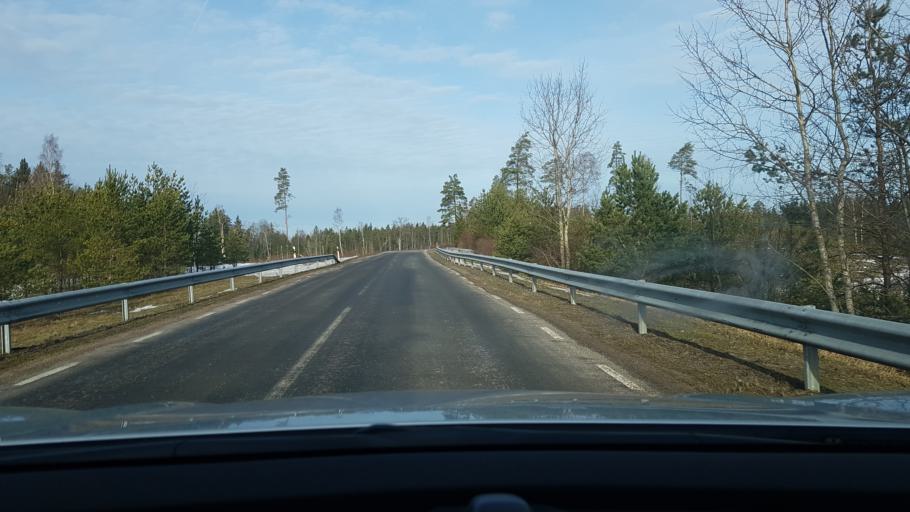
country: EE
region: Saare
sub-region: Kuressaare linn
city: Kuressaare
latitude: 58.4601
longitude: 22.7054
